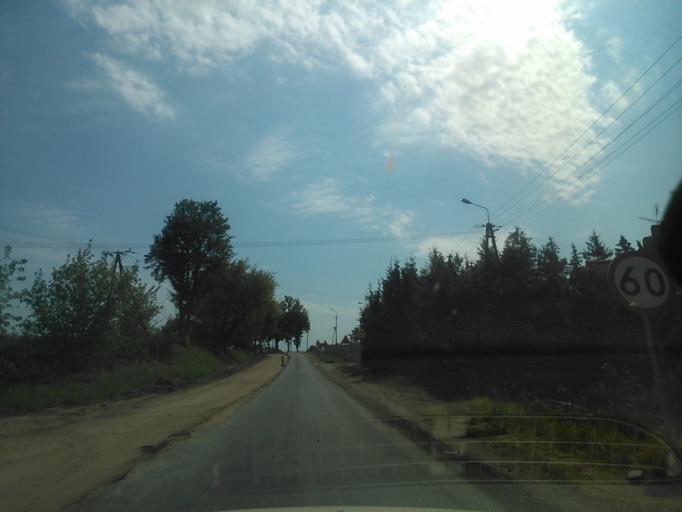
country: PL
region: Warmian-Masurian Voivodeship
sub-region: Powiat dzialdowski
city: Dzialdowo
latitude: 53.2298
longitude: 20.1918
